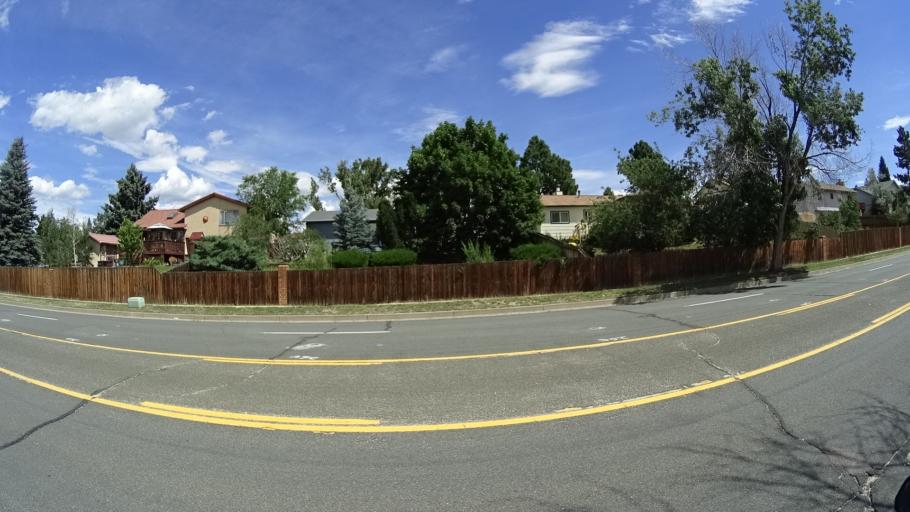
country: US
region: Colorado
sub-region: El Paso County
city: Black Forest
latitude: 38.9430
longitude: -104.7578
